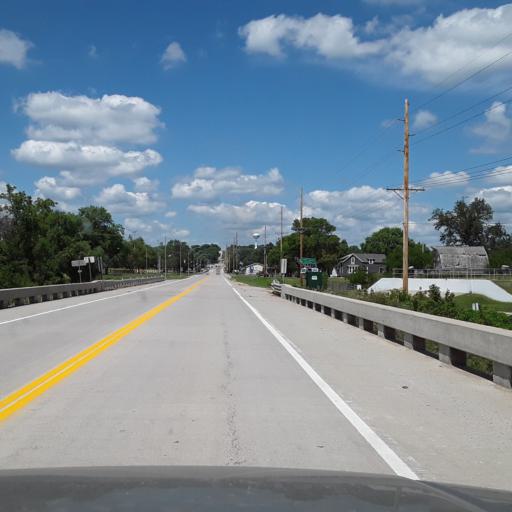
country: US
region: Nebraska
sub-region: Nance County
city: Genoa
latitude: 41.4409
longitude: -97.7346
